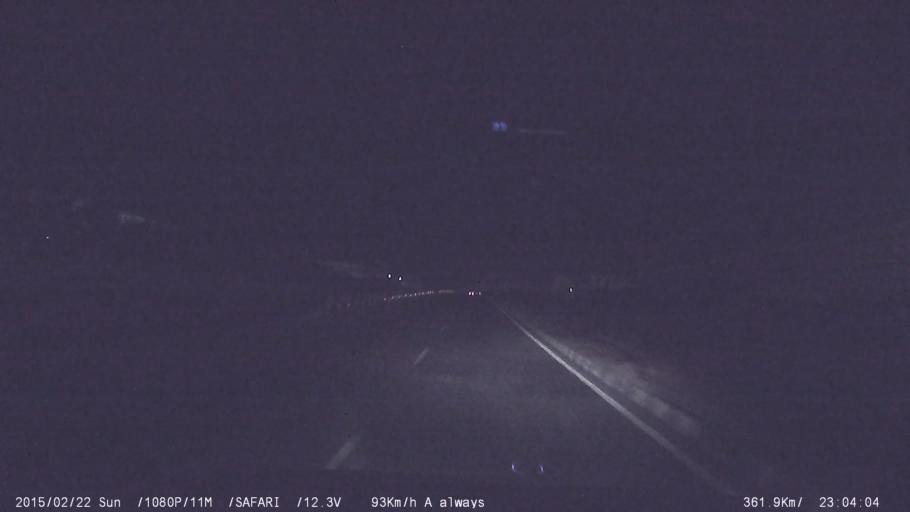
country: IN
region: Tamil Nadu
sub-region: Namakkal
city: Rasipuram
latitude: 11.3974
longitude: 78.1603
